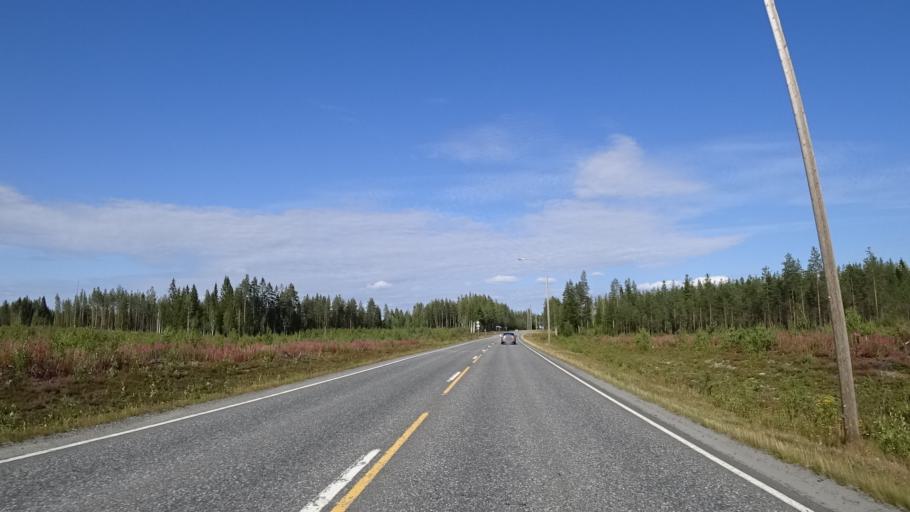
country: FI
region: North Karelia
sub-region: Joensuu
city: Eno
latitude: 62.7699
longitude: 30.0466
